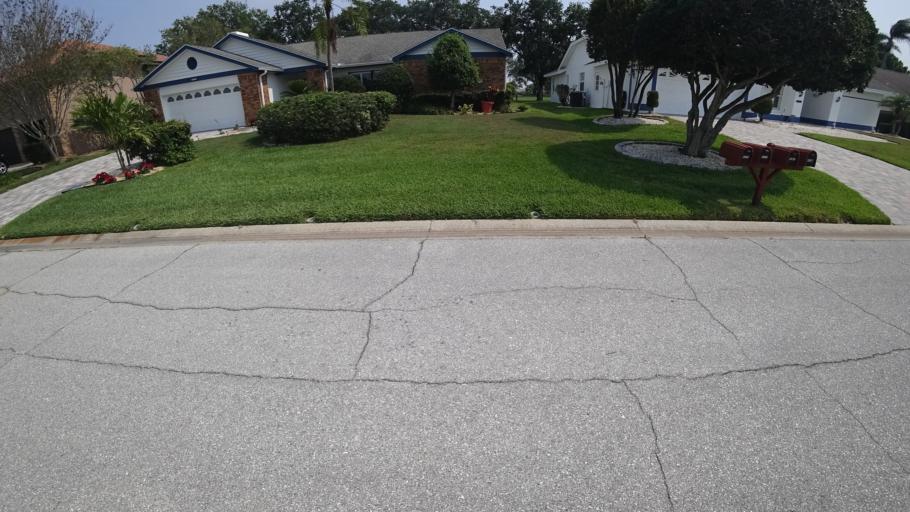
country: US
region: Florida
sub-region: Manatee County
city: Samoset
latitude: 27.4527
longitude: -82.5095
